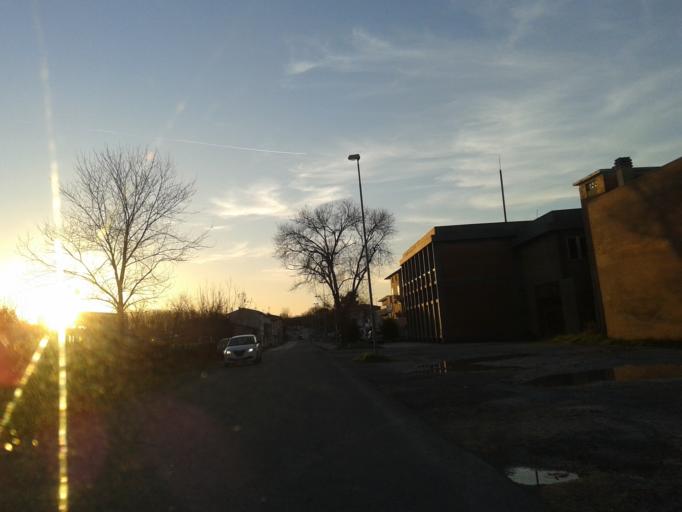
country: IT
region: Tuscany
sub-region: Provincia di Livorno
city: Guasticce
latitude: 43.5959
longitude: 10.3545
